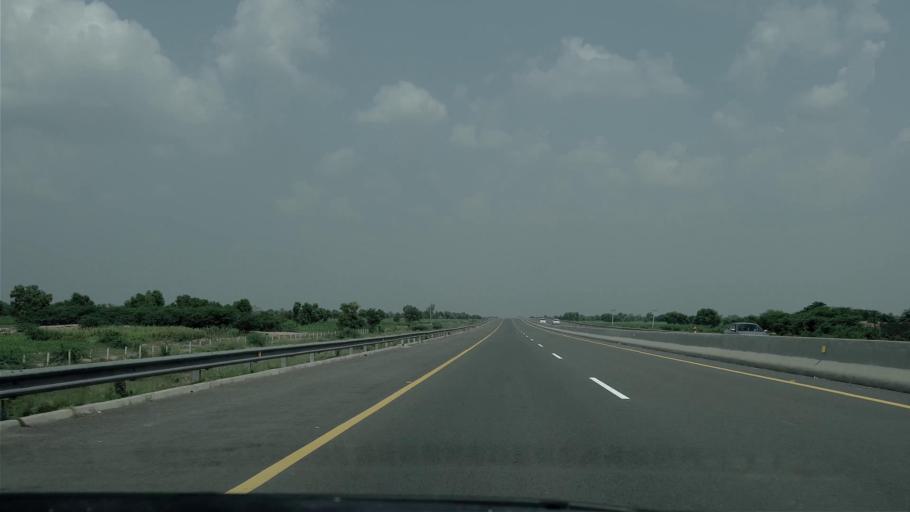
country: PK
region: Punjab
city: Gojra
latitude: 31.1966
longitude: 72.6552
